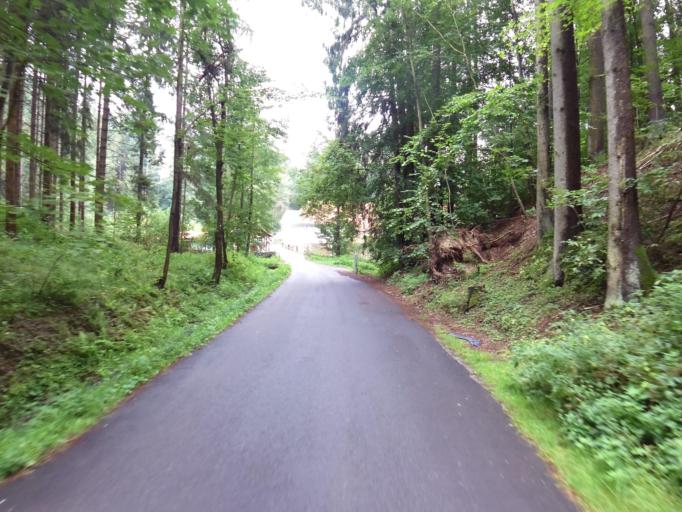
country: CZ
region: Jihocesky
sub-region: Okres Ceske Budejovice
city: Nove Hrady
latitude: 48.7831
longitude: 14.7883
